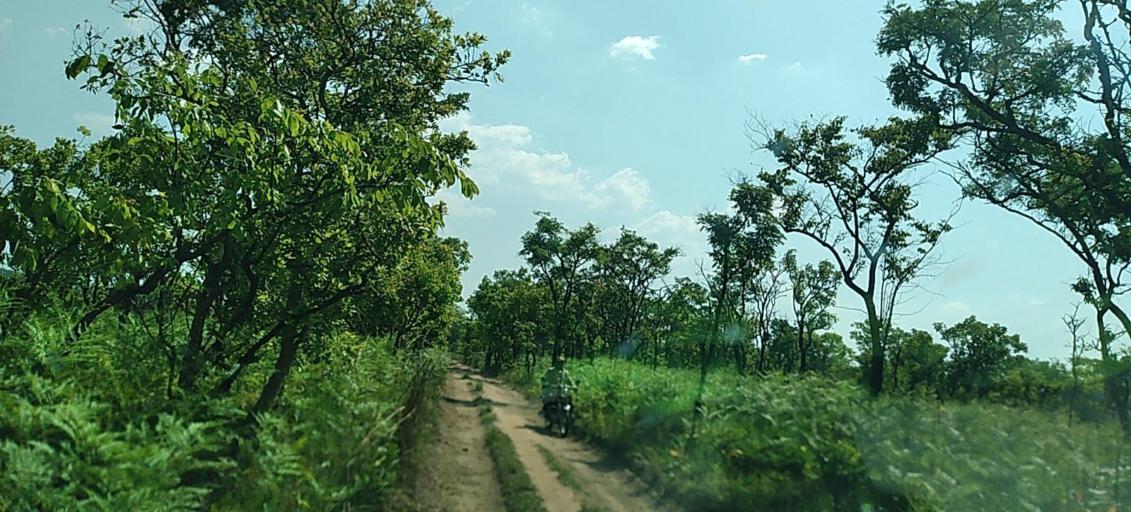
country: CD
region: Katanga
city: Kolwezi
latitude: -11.2639
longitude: 25.0028
